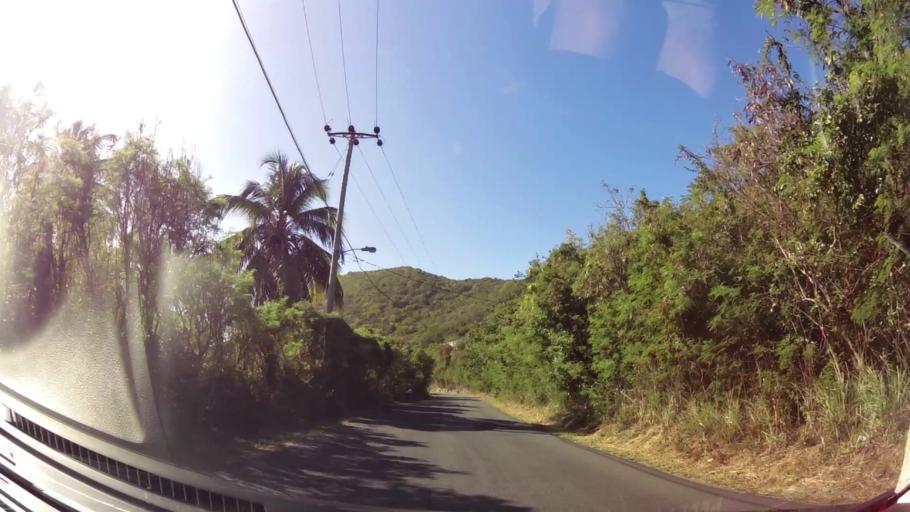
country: VG
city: Road Town
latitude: 18.3878
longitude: -64.6993
